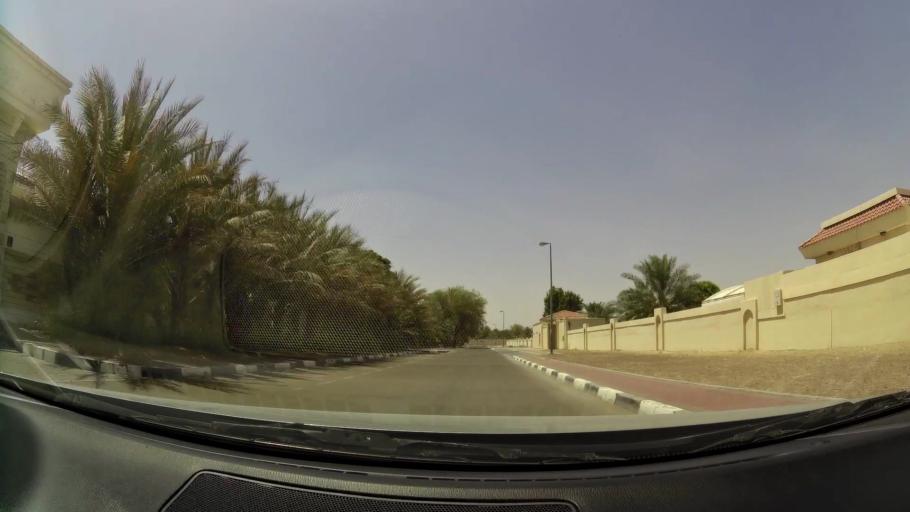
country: OM
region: Al Buraimi
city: Al Buraymi
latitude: 24.2801
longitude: 55.7512
